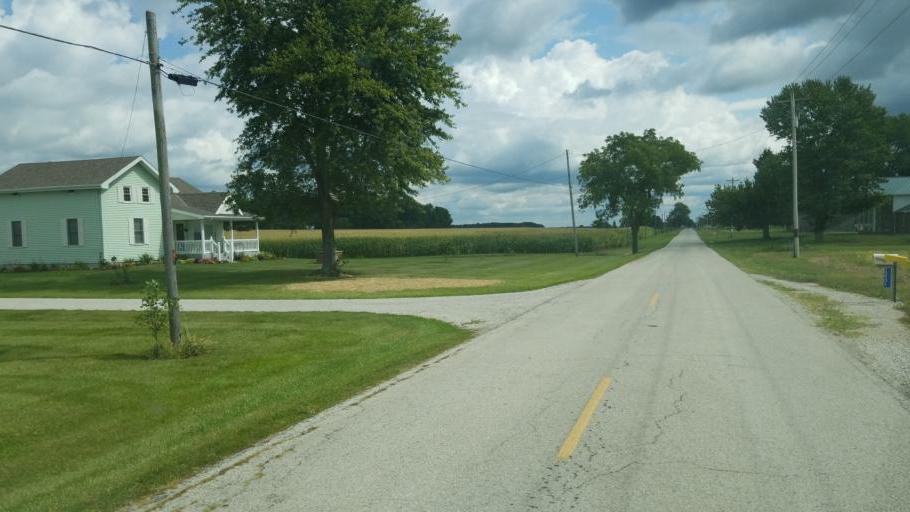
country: US
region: Ohio
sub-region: Sandusky County
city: Mount Carmel
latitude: 41.0954
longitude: -82.9099
